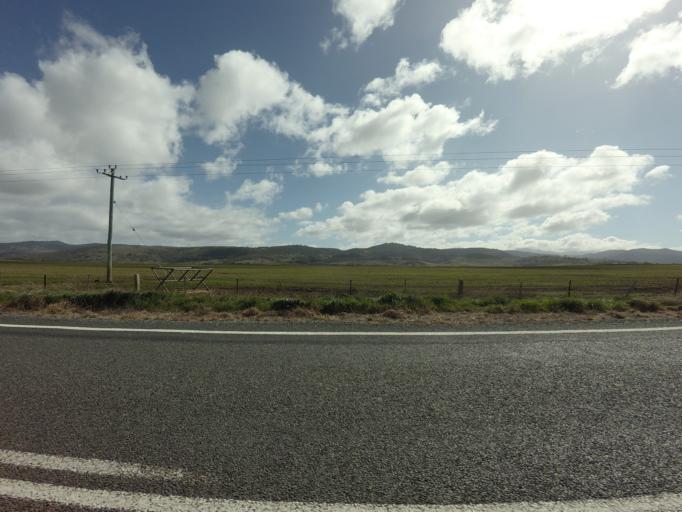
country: AU
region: Tasmania
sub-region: Northern Midlands
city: Evandale
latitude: -41.8028
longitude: 147.6860
